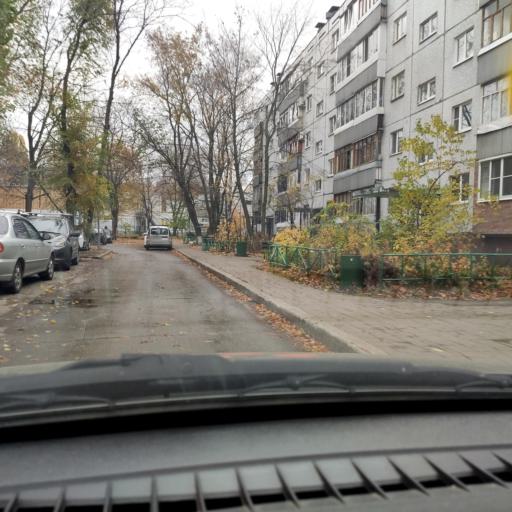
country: RU
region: Samara
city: Tol'yatti
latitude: 53.5129
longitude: 49.2861
